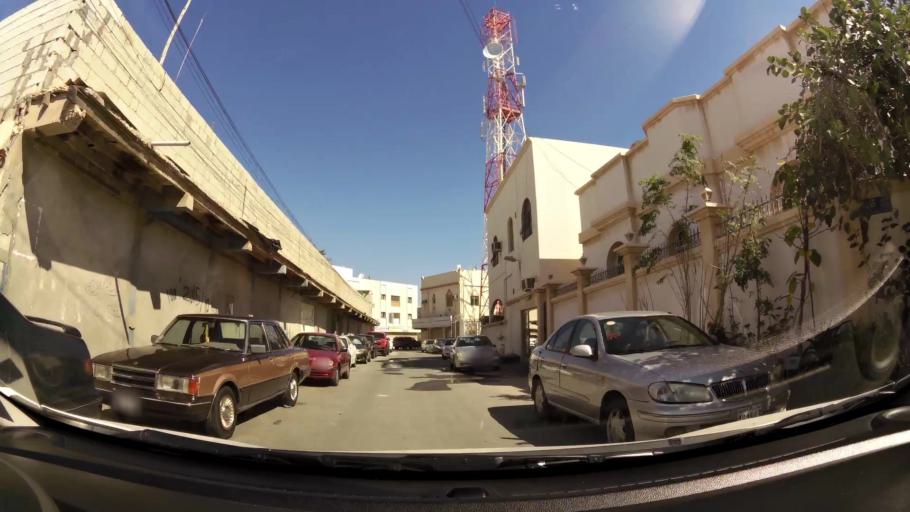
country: BH
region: Muharraq
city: Al Muharraq
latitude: 26.2434
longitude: 50.6147
